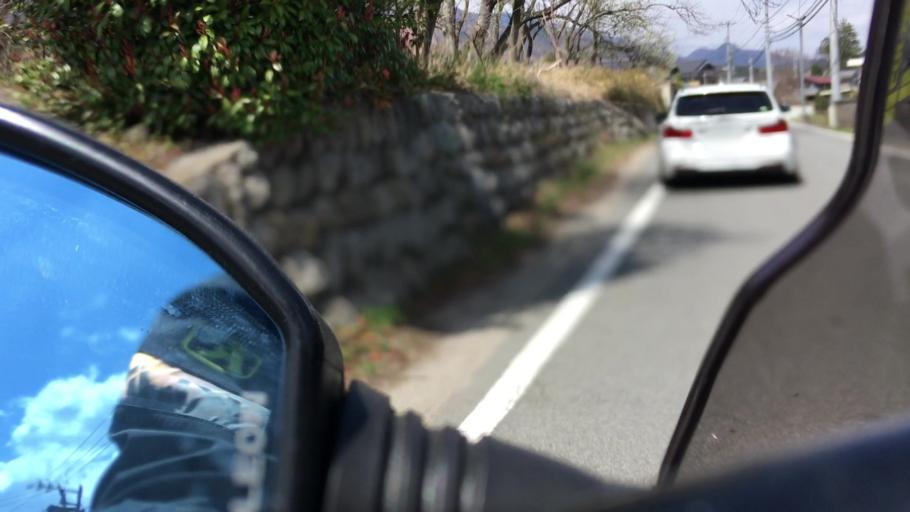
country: JP
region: Yamanashi
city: Nirasaki
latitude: 35.7896
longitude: 138.3220
